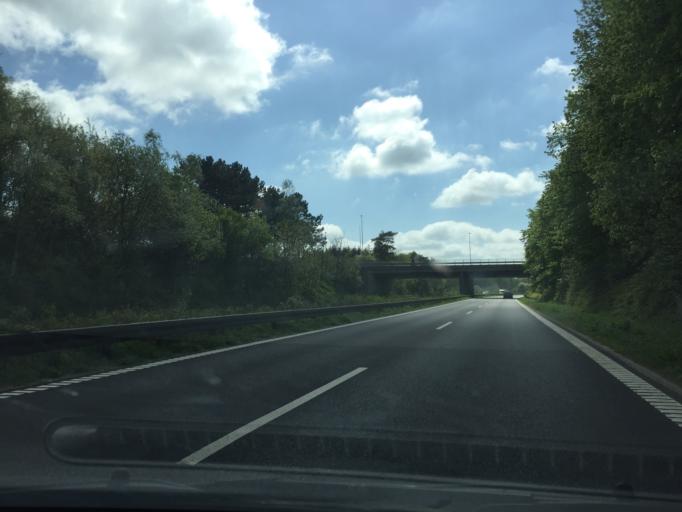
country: DK
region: Zealand
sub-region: Guldborgsund Kommune
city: Sakskobing
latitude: 54.7951
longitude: 11.6608
